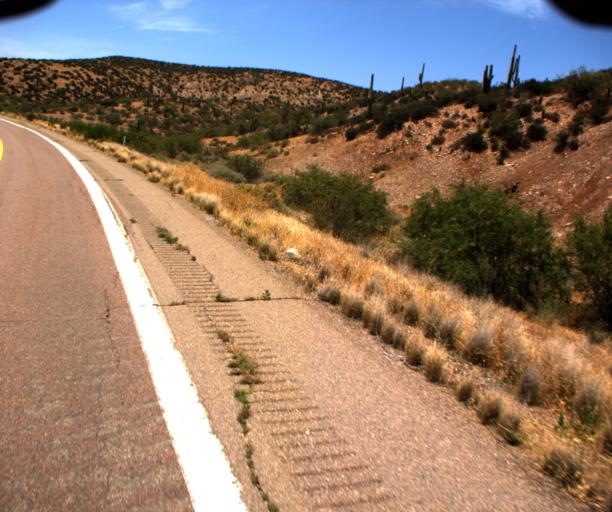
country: US
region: Arizona
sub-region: Gila County
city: Tonto Basin
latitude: 33.8034
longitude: -111.2739
